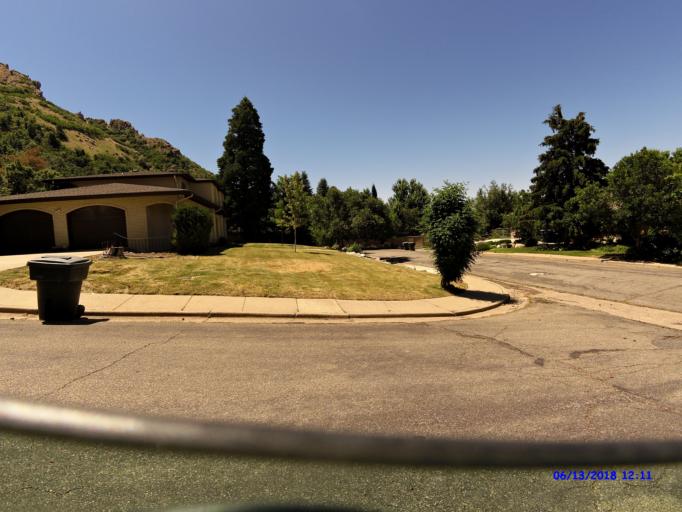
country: US
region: Utah
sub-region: Weber County
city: Ogden
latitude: 41.2132
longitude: -111.9306
